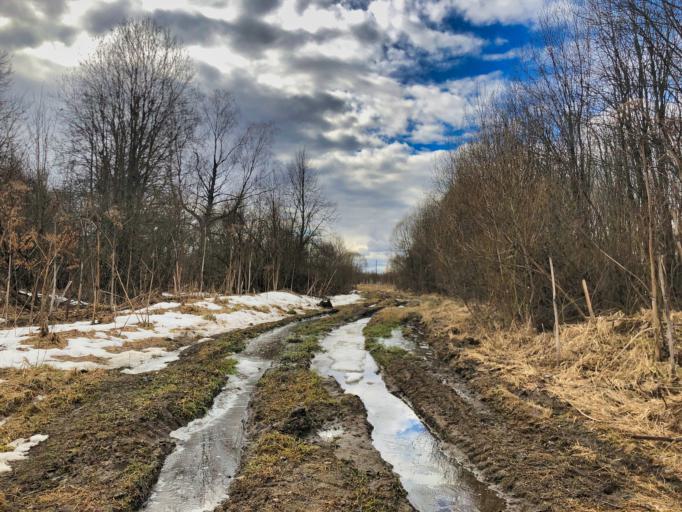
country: RU
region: Tverskaya
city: Rzhev
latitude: 56.2240
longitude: 34.3012
